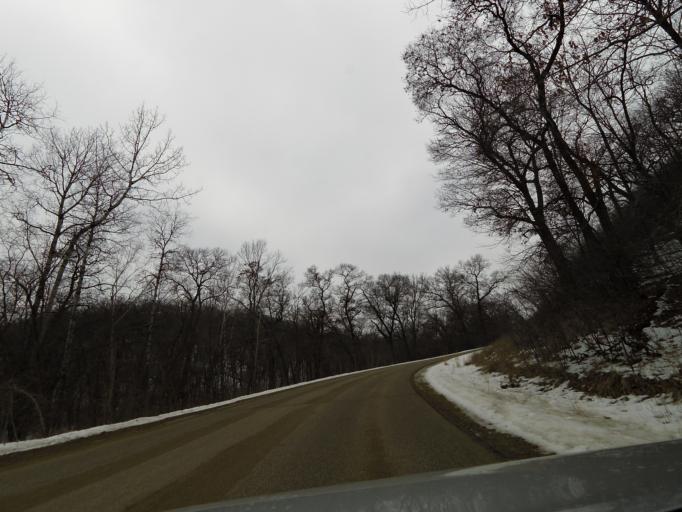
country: US
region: Minnesota
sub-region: Washington County
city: Afton
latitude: 44.8439
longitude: -92.7888
